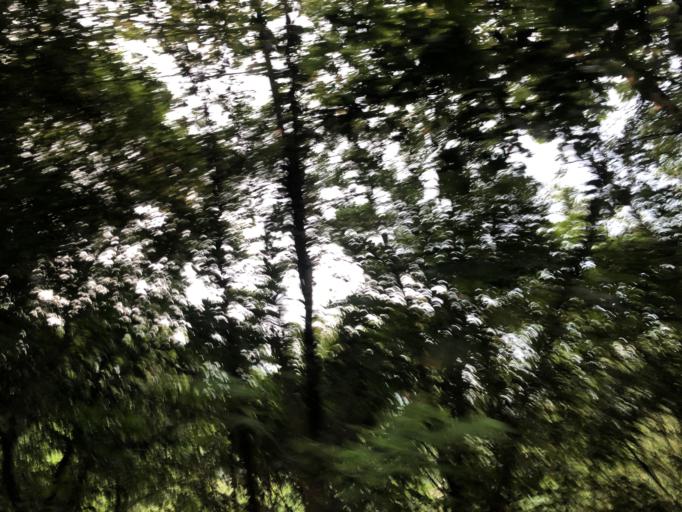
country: TW
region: Taiwan
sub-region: Keelung
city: Keelung
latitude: 25.1544
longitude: 121.6458
